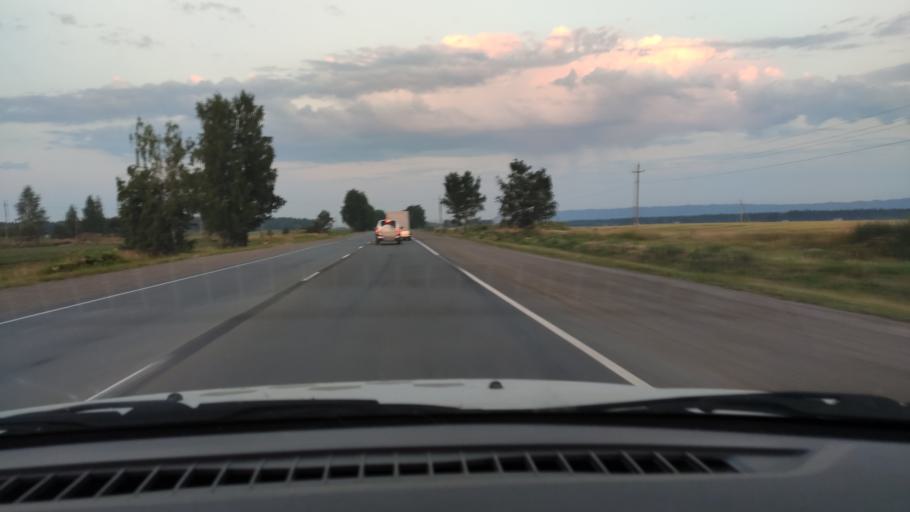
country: RU
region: Perm
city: Ust'-Kachka
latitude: 58.0590
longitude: 55.6091
